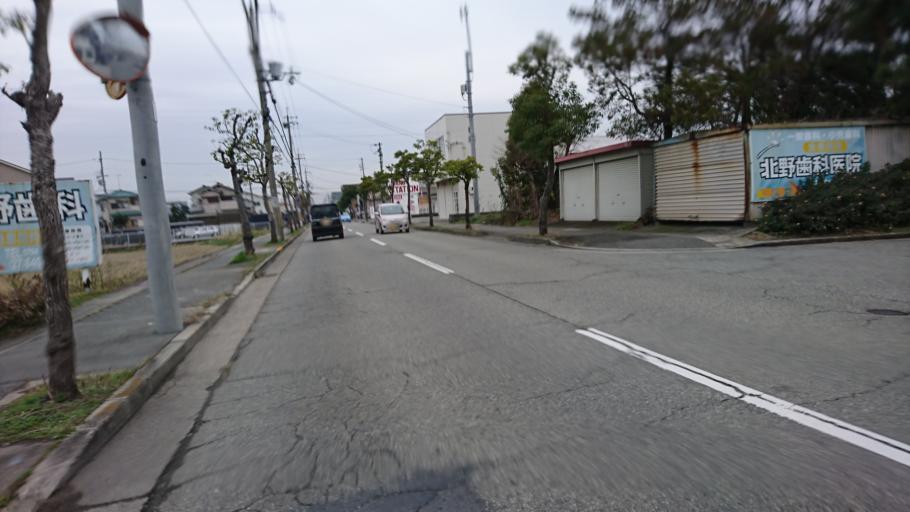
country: JP
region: Hyogo
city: Kakogawacho-honmachi
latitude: 34.7637
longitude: 134.8173
